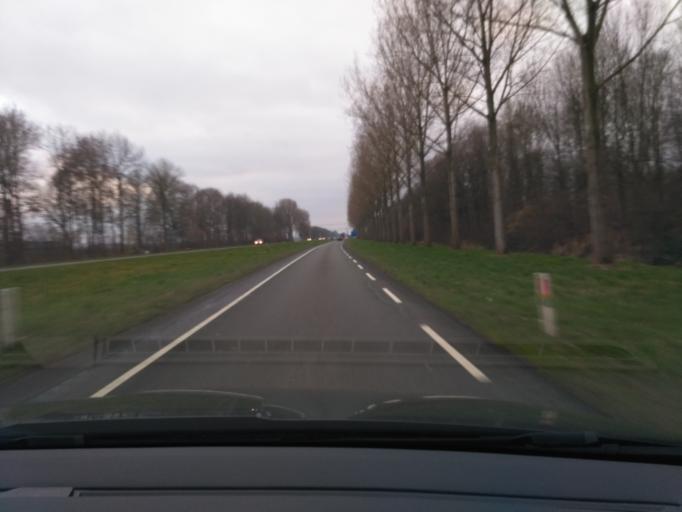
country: NL
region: Flevoland
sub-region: Gemeente Dronten
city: Dronten
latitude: 52.5116
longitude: 5.7301
